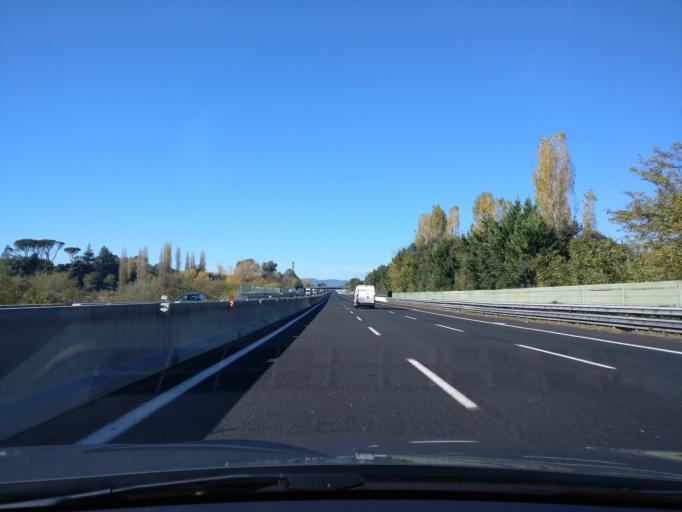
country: IT
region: Latium
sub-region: Provincia di Frosinone
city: Ceprano
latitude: 41.5430
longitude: 13.5166
